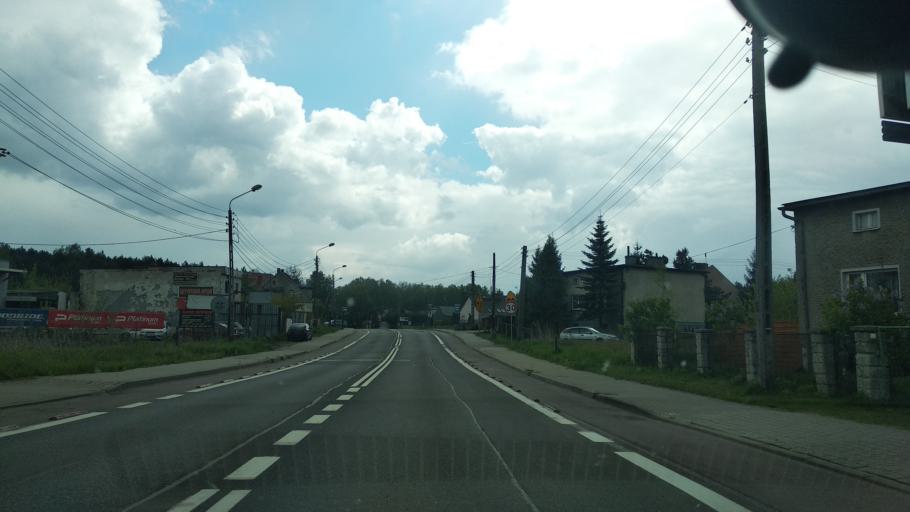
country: PL
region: Silesian Voivodeship
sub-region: Ruda Slaska
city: Ruda Slaska
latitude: 50.2392
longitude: 18.9078
